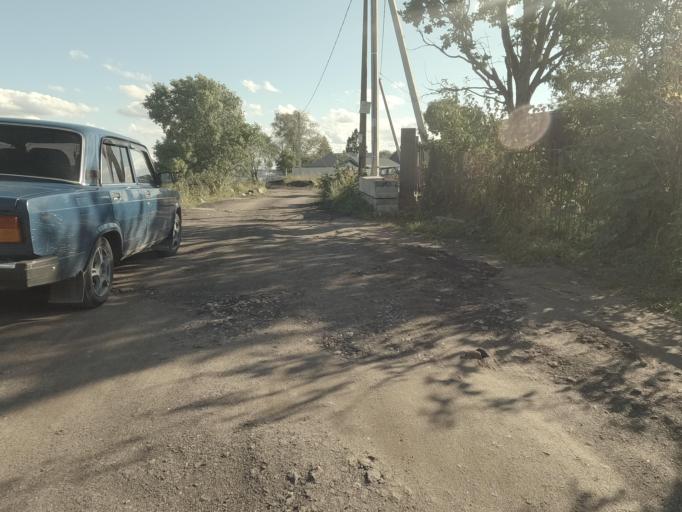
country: RU
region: Leningrad
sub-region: Volosovskiy Rayon
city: Shlissel'burg
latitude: 59.9532
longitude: 31.0264
